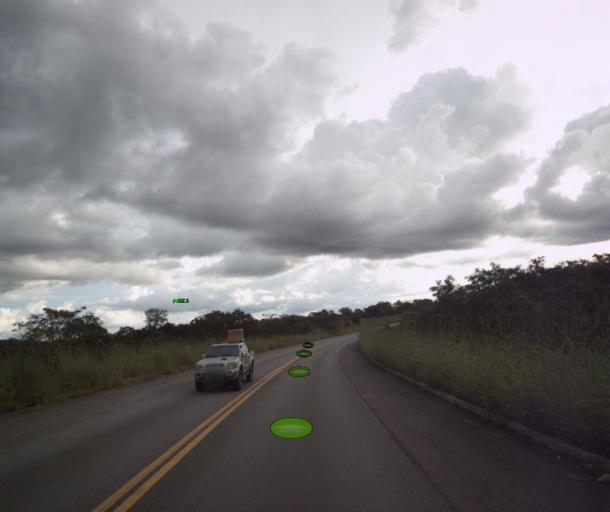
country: BR
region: Goias
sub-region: Niquelandia
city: Niquelandia
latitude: -14.4993
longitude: -48.4947
